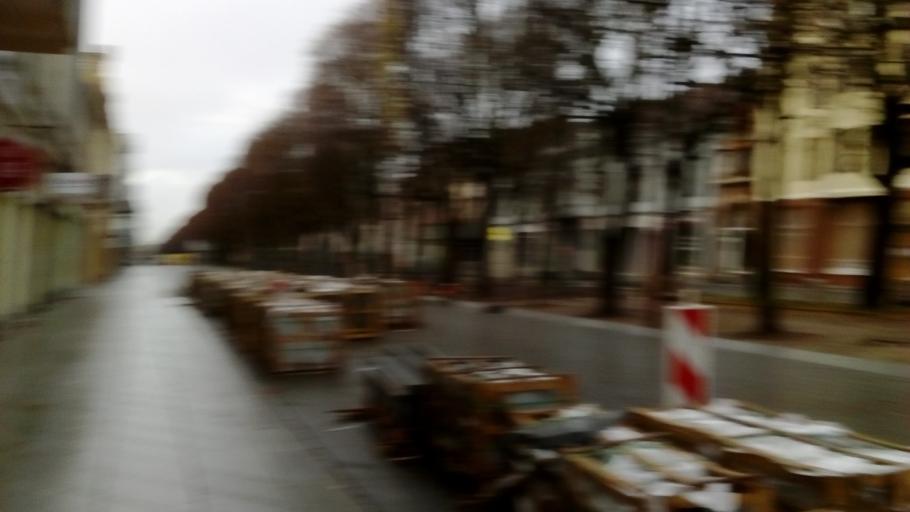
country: LT
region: Kauno apskritis
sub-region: Kaunas
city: Kaunas
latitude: 54.8985
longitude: 23.9177
